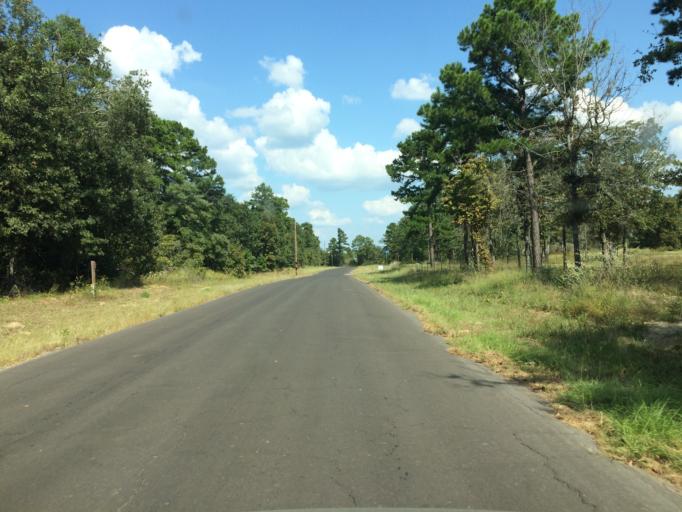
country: US
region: Texas
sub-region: Wood County
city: Hawkins
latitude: 32.6579
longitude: -95.2093
